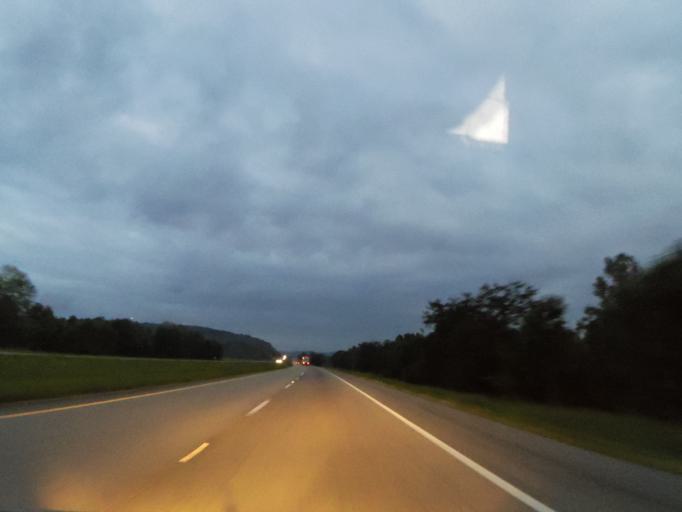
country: US
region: Alabama
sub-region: Madison County
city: New Hope
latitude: 34.6146
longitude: -86.2886
